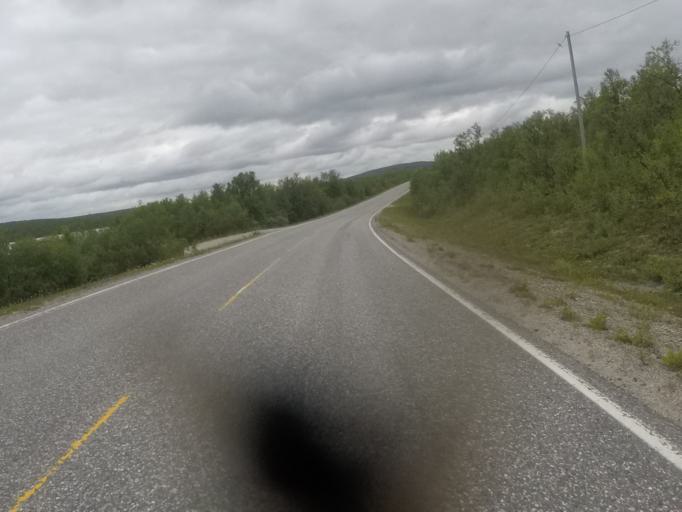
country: NO
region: Finnmark Fylke
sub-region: Kautokeino
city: Kautokeino
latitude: 68.9501
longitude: 23.0884
